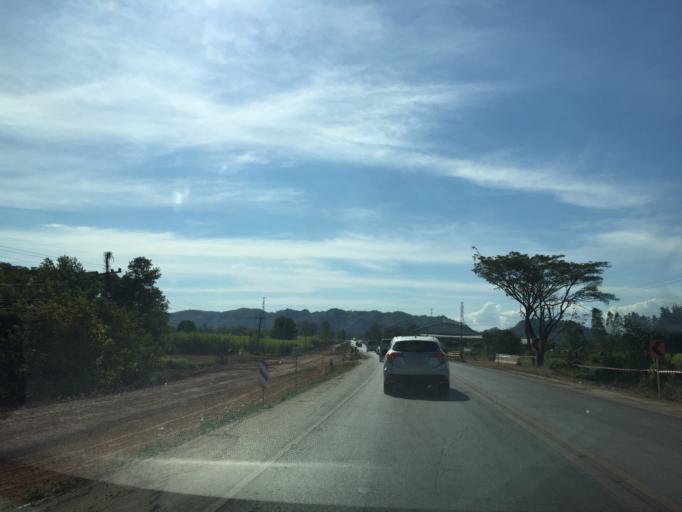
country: TH
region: Loei
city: Wang Saphung
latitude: 17.2986
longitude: 101.8571
